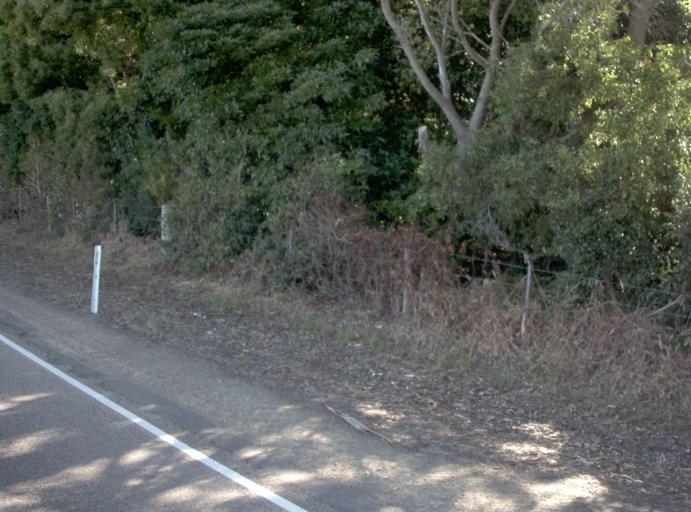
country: AU
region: Victoria
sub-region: East Gippsland
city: Lakes Entrance
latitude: -37.7353
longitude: 148.5048
